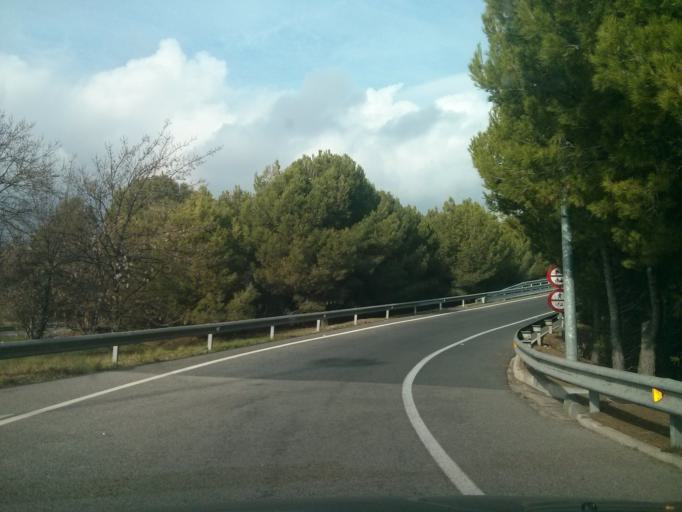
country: ES
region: Catalonia
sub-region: Provincia de Tarragona
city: El Vendrell
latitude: 41.1941
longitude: 1.5395
